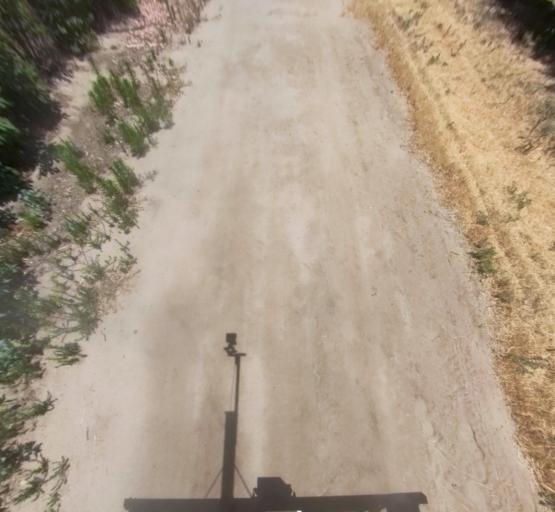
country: US
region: California
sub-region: Madera County
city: Parkwood
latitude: 36.8356
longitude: -120.1695
